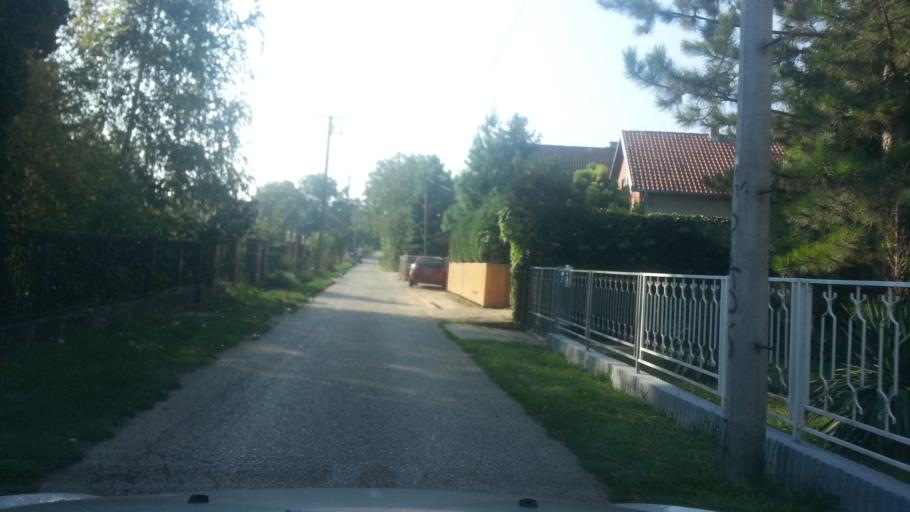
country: RS
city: Novi Banovci
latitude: 44.9626
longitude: 20.2831
